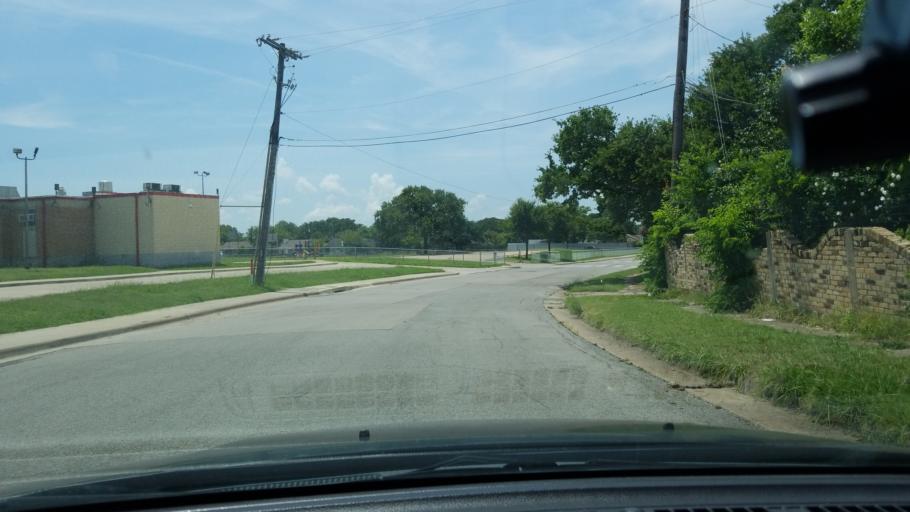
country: US
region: Texas
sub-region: Dallas County
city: Balch Springs
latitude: 32.7415
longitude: -96.6419
